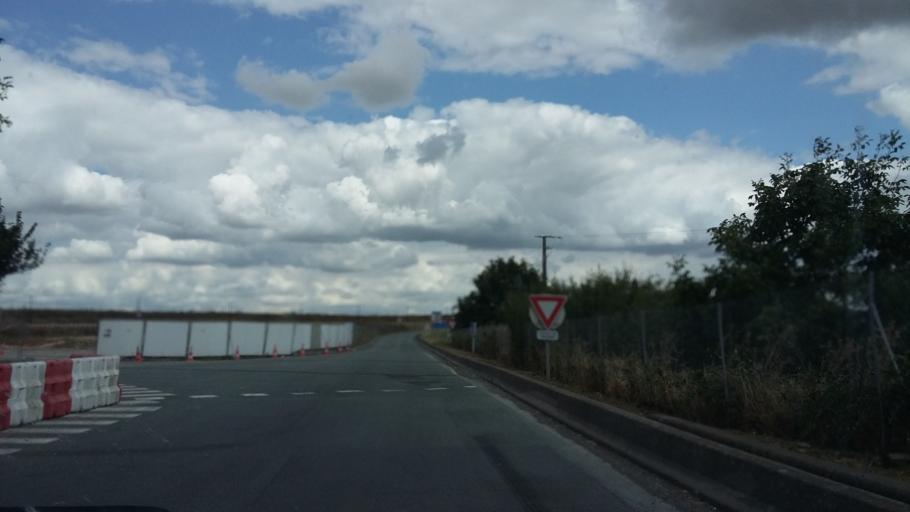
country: FR
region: Poitou-Charentes
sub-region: Departement de la Vienne
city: Jaunay-Clan
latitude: 46.7027
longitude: 0.3724
